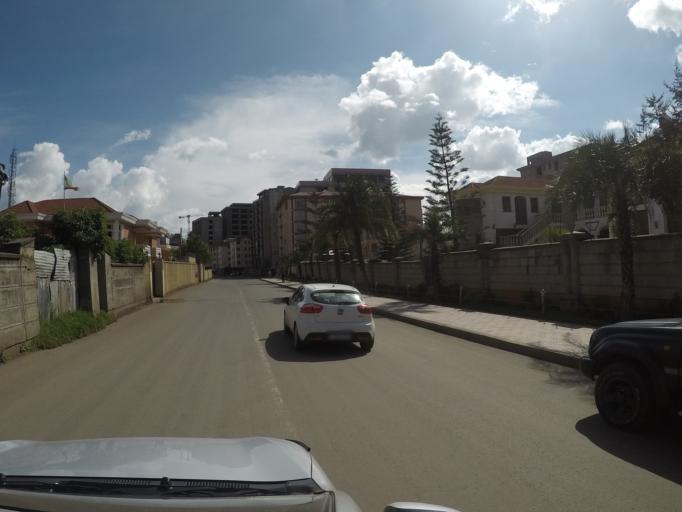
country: ET
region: Adis Abeba
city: Addis Ababa
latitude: 8.9936
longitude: 38.7895
